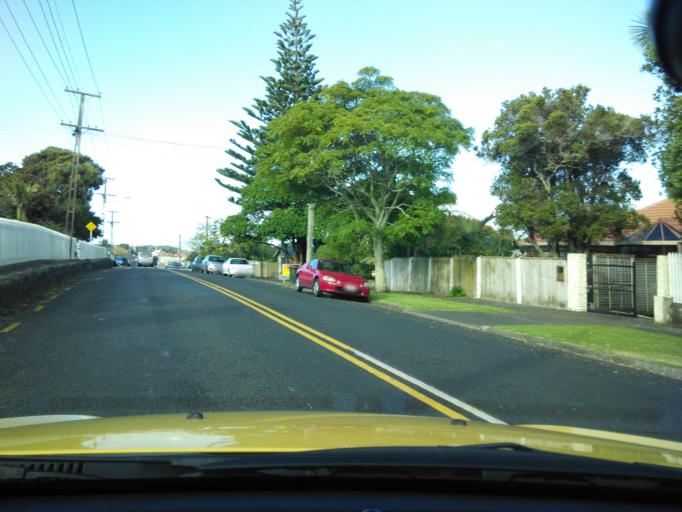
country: NZ
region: Auckland
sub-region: Auckland
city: Mangere
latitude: -36.9212
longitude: 174.7788
